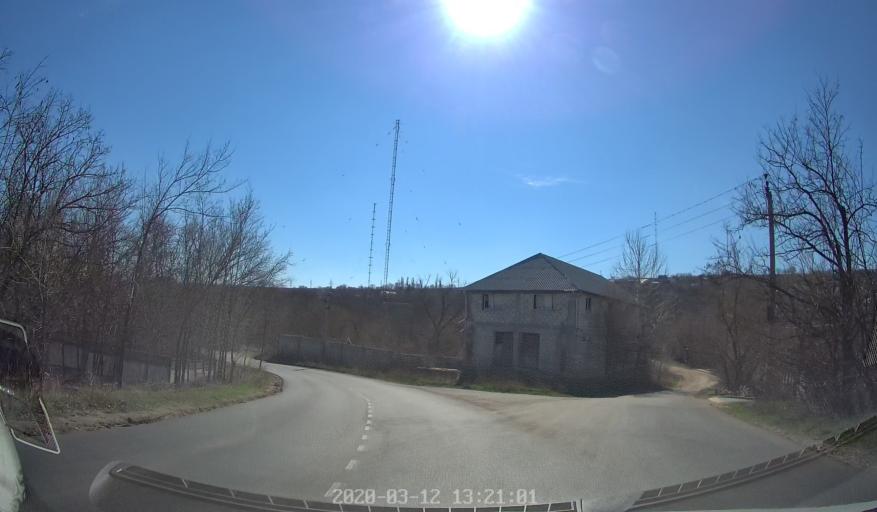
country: MD
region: Laloveni
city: Ialoveni
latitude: 46.9559
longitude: 28.8302
